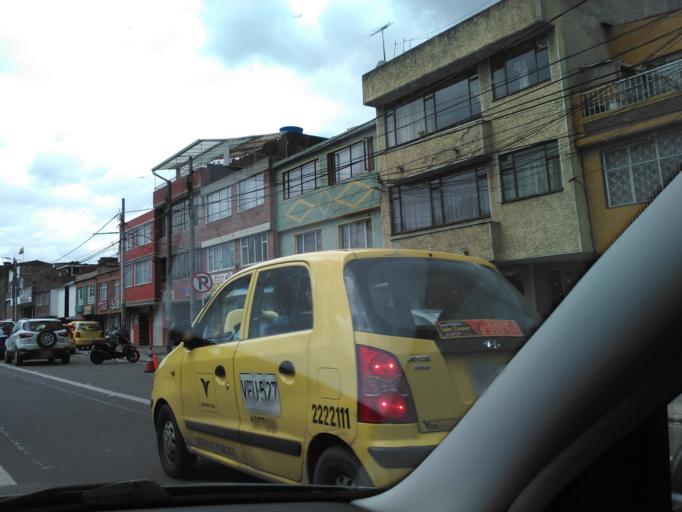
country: CO
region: Bogota D.C.
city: Bogota
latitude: 4.6217
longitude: -74.1109
